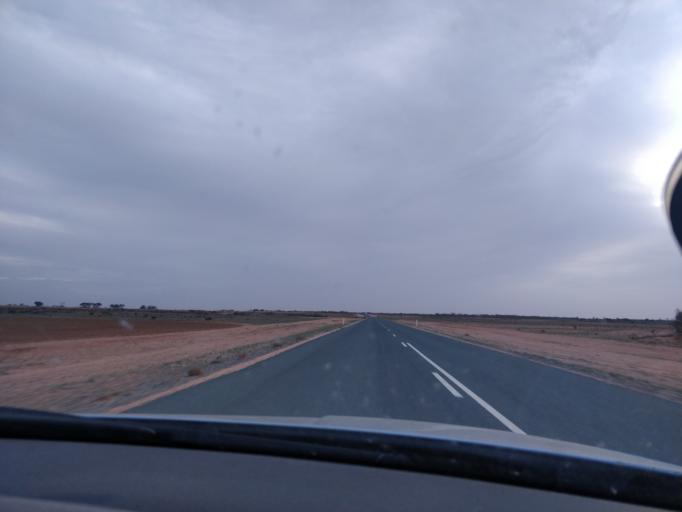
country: AU
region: New South Wales
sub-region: Wentworth
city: Gol Gol
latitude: -34.0454
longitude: 142.3381
